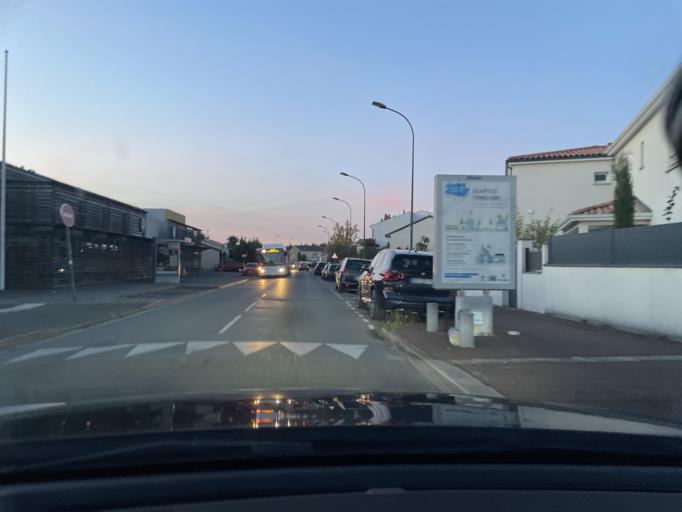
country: FR
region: Aquitaine
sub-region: Departement de la Gironde
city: Le Bouscat
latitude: 44.8824
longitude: -0.5930
